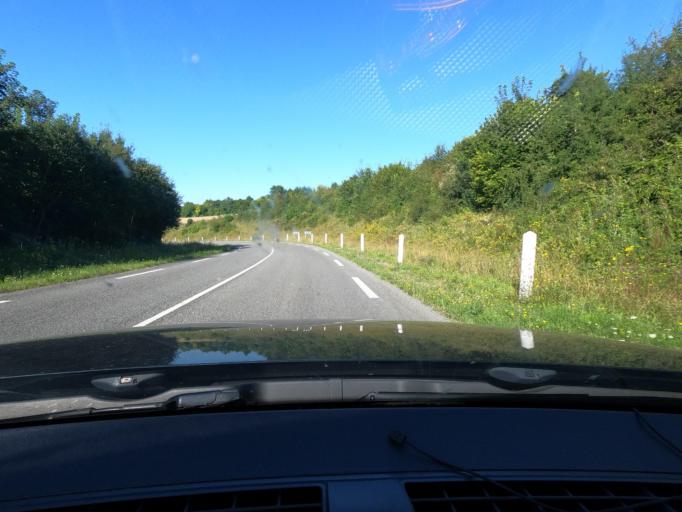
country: FR
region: Picardie
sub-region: Departement de la Somme
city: Poix-de-Picardie
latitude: 49.7904
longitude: 1.9746
